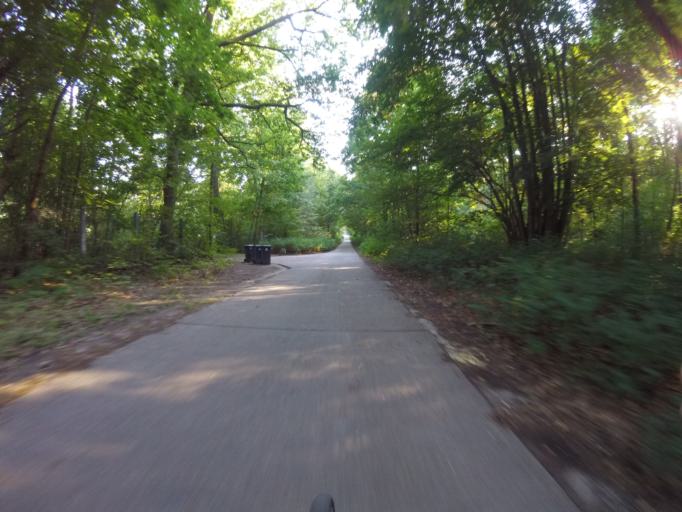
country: DE
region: Brandenburg
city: Strausberg
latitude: 52.5780
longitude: 13.8250
